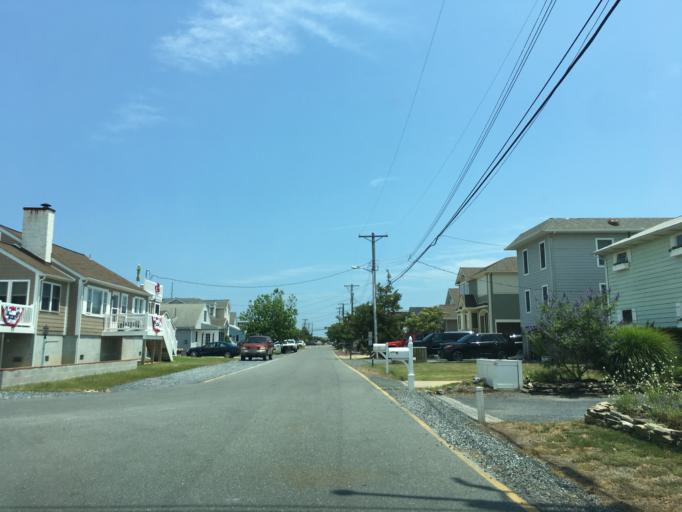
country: US
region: Delaware
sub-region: Sussex County
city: Bethany Beach
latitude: 38.4624
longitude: -75.0544
